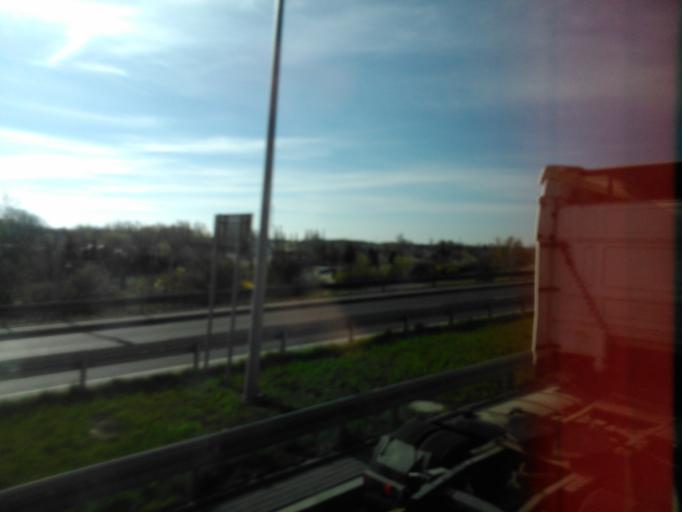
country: PL
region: Kujawsko-Pomorskie
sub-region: Torun
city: Torun
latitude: 52.9993
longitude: 18.6549
